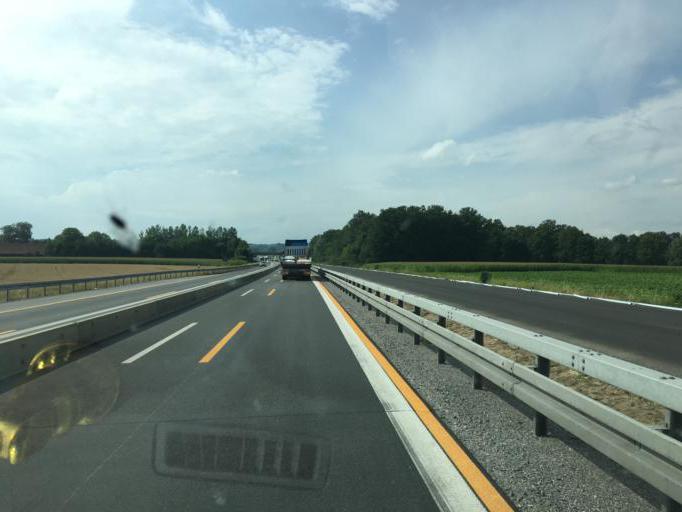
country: DE
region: Bavaria
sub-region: Lower Bavaria
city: Niederwinkling
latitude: 48.8862
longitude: 12.8261
